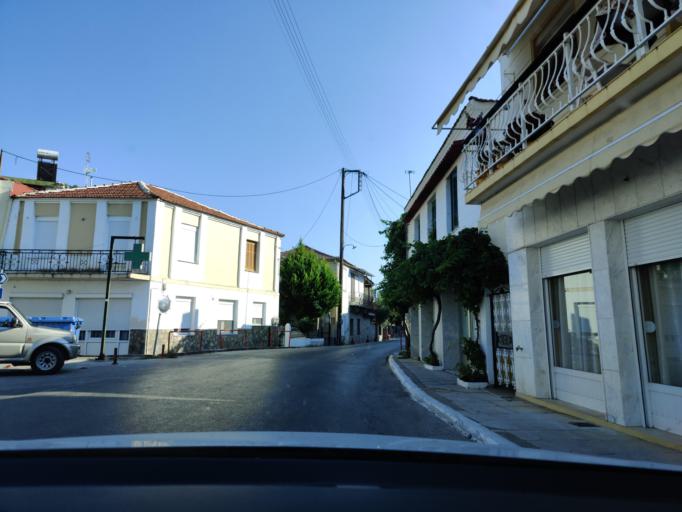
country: GR
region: East Macedonia and Thrace
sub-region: Nomos Kavalas
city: Prinos
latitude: 40.7079
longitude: 24.5342
